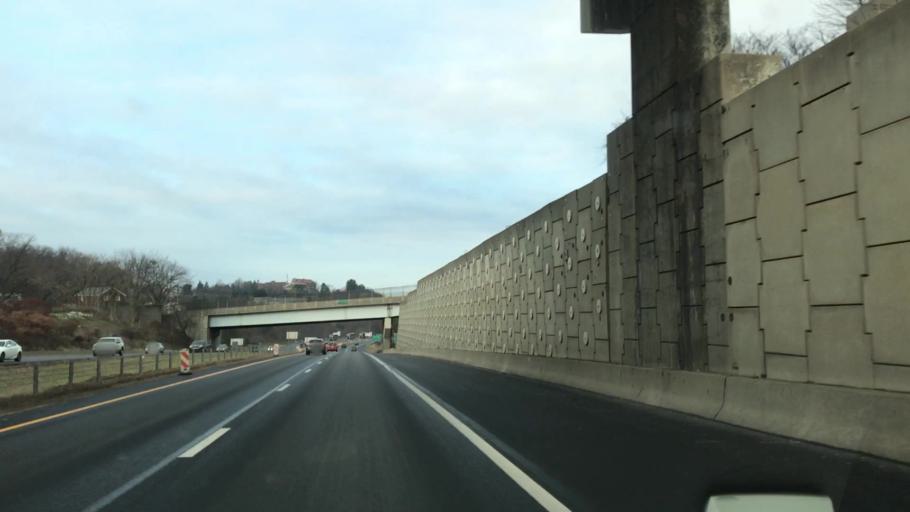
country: US
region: Pennsylvania
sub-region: Allegheny County
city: West View
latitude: 40.5073
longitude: -80.0371
